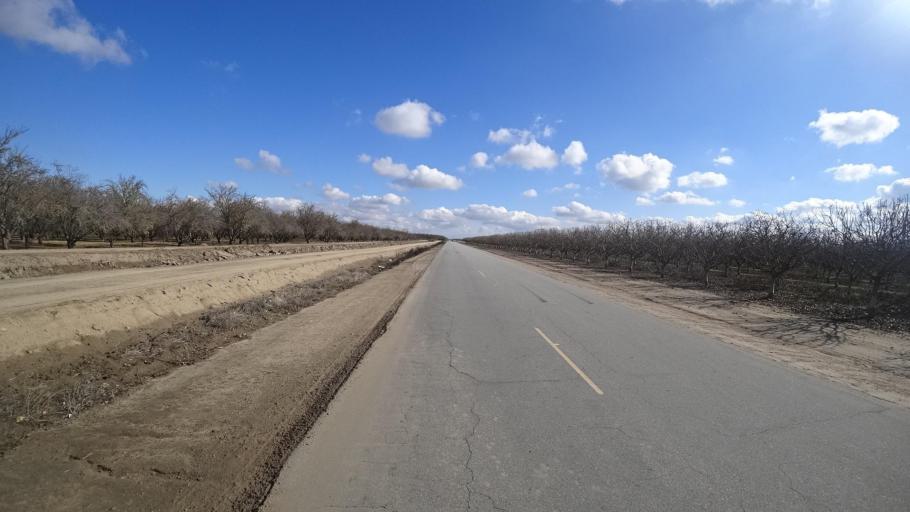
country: US
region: California
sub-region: Kern County
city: Wasco
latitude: 35.6742
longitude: -119.3159
